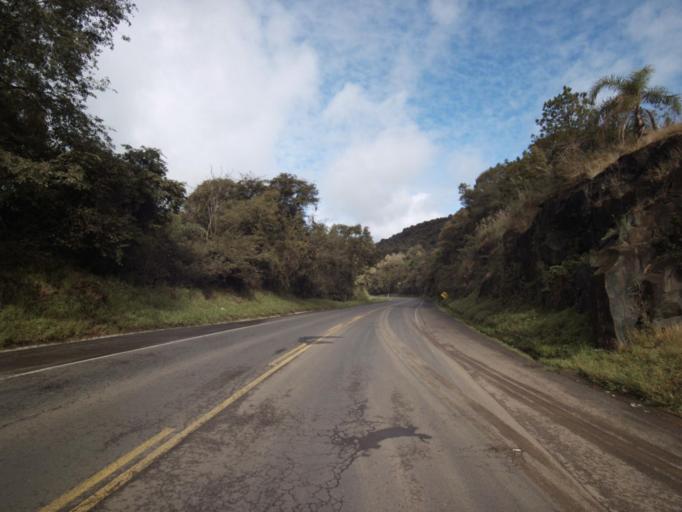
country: BR
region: Santa Catarina
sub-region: Concordia
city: Concordia
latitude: -27.2061
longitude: -51.9498
